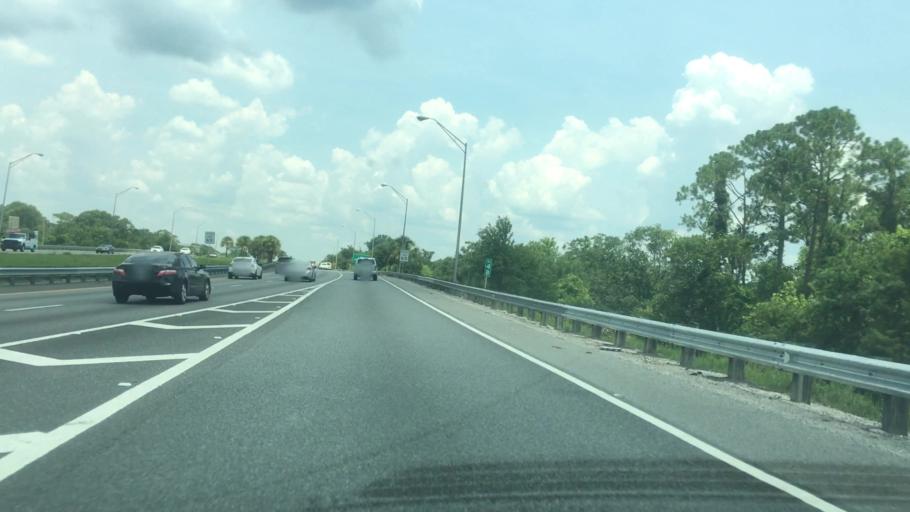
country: US
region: Florida
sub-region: Duval County
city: Jacksonville
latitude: 30.3282
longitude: -81.5286
